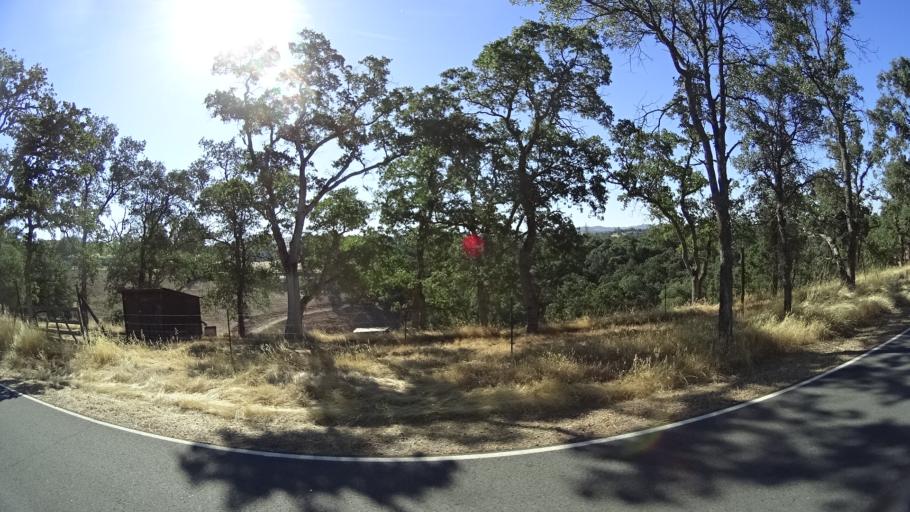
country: US
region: California
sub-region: Calaveras County
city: Rancho Calaveras
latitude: 38.1181
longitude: -120.8685
